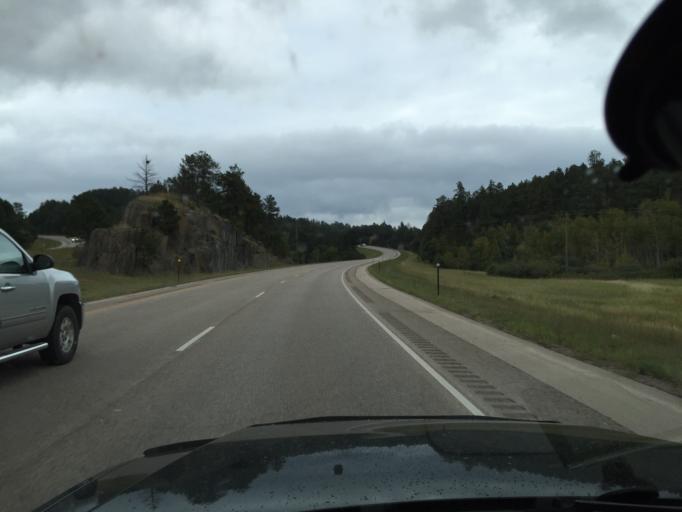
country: US
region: South Dakota
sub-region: Pennington County
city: Colonial Pine Hills
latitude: 43.9425
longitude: -103.3894
